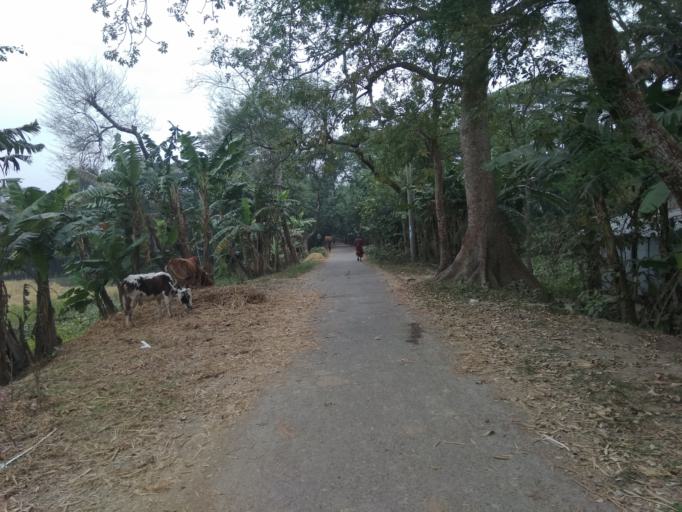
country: BD
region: Barisal
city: Mehendiganj
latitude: 22.9180
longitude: 90.3912
